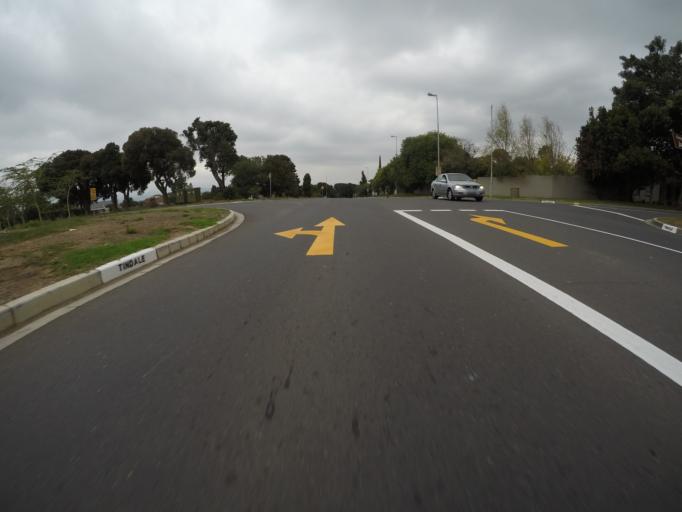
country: ZA
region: Western Cape
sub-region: City of Cape Town
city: Kraaifontein
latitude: -33.8436
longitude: 18.6435
